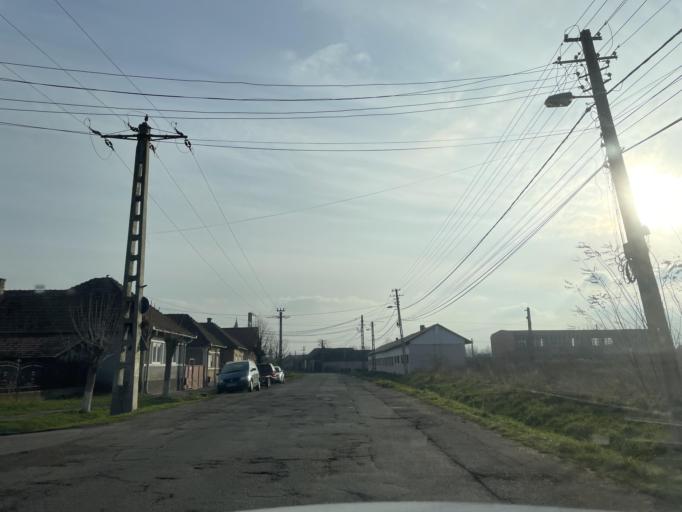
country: RO
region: Mures
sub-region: Municipiul Reghin
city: Apalina
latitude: 46.7526
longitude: 24.6932
